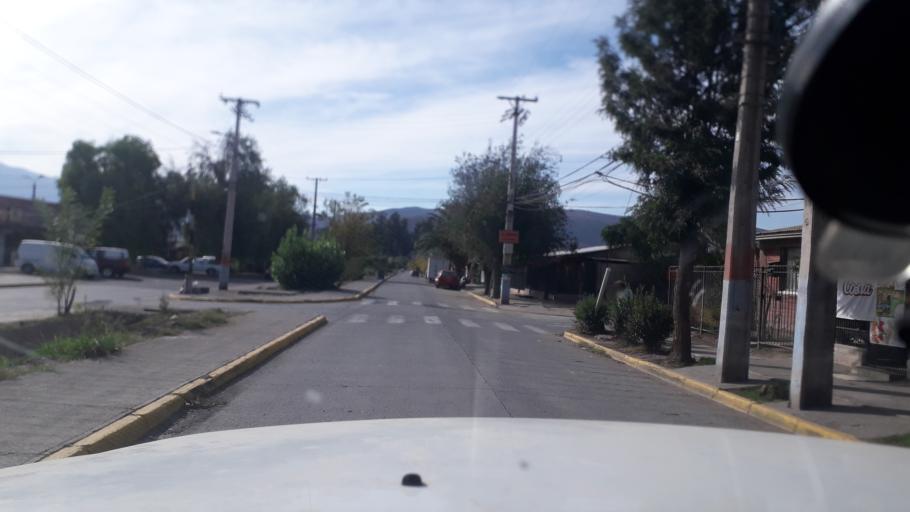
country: CL
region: Valparaiso
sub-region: Provincia de San Felipe
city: San Felipe
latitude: -32.7426
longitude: -70.7107
